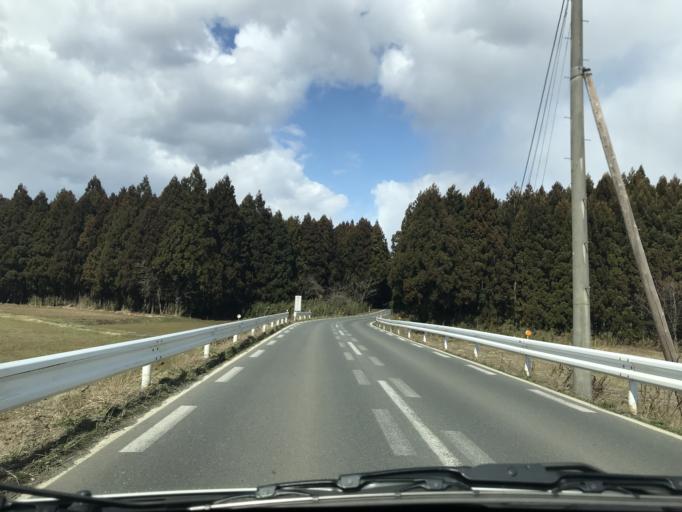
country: JP
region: Iwate
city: Kitakami
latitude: 39.2873
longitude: 141.0678
